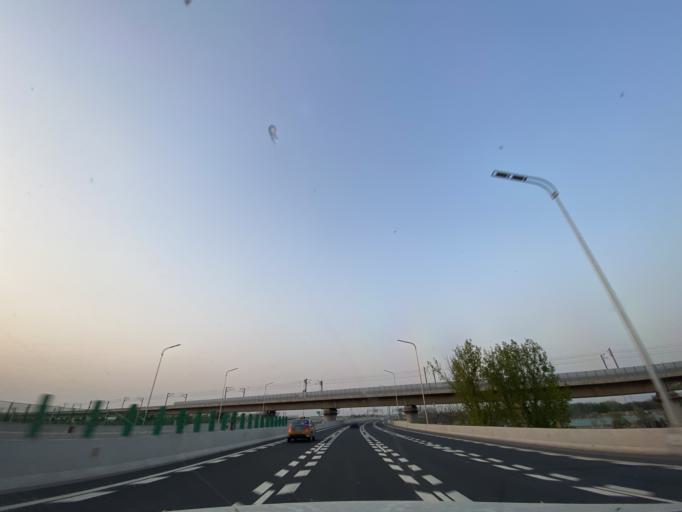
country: CN
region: Beijing
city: Xingfeng
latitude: 39.6847
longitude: 116.3633
